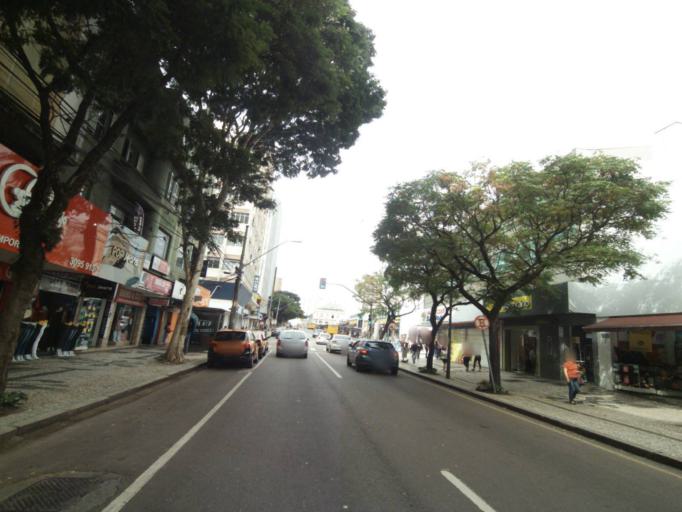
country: BR
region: Parana
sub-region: Curitiba
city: Curitiba
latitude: -25.4341
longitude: -49.2722
